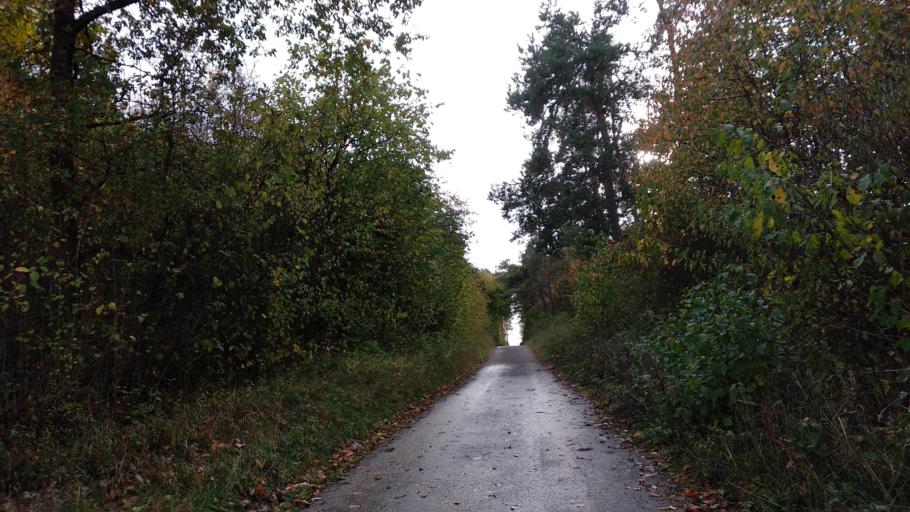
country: DE
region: North Rhine-Westphalia
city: Beverungen
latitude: 51.6946
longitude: 9.3364
